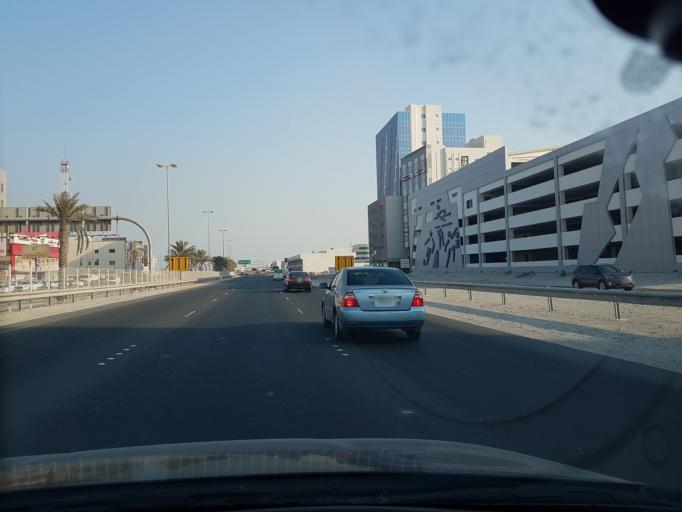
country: BH
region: Northern
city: Ar Rifa'
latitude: 26.1360
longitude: 50.5839
